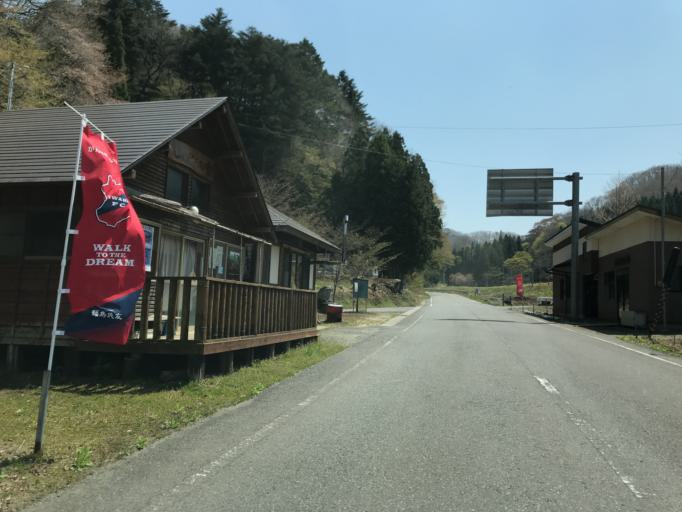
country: JP
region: Fukushima
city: Ishikawa
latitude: 36.9874
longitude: 140.6175
